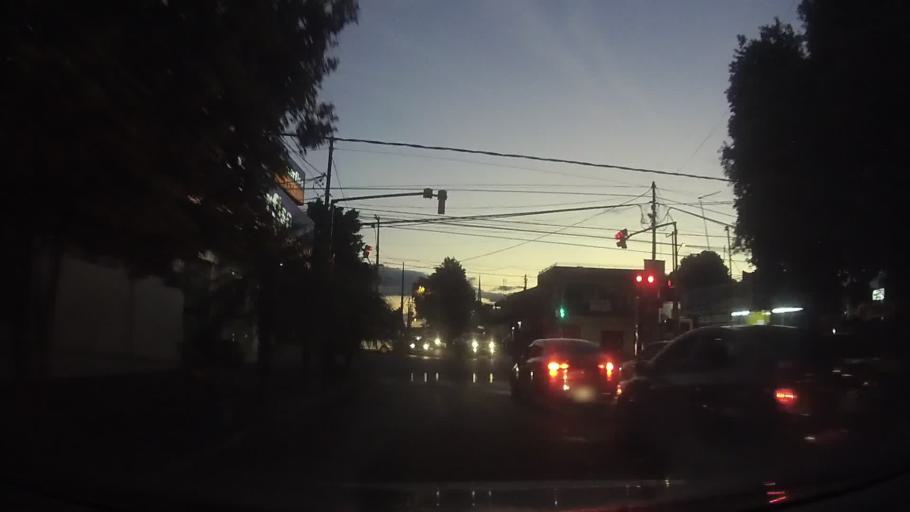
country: PY
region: Central
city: Itaugua
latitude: -25.3920
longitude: -57.3547
